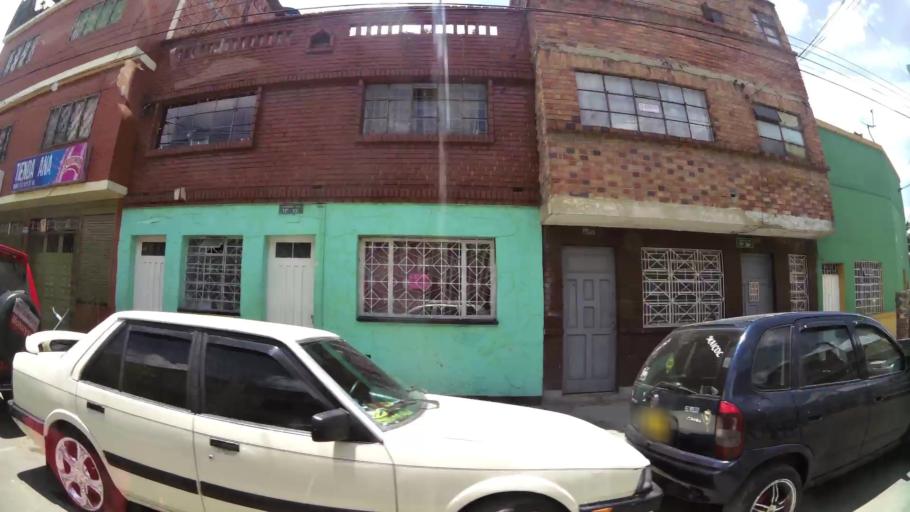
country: CO
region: Bogota D.C.
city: Bogota
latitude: 4.5900
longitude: -74.1077
